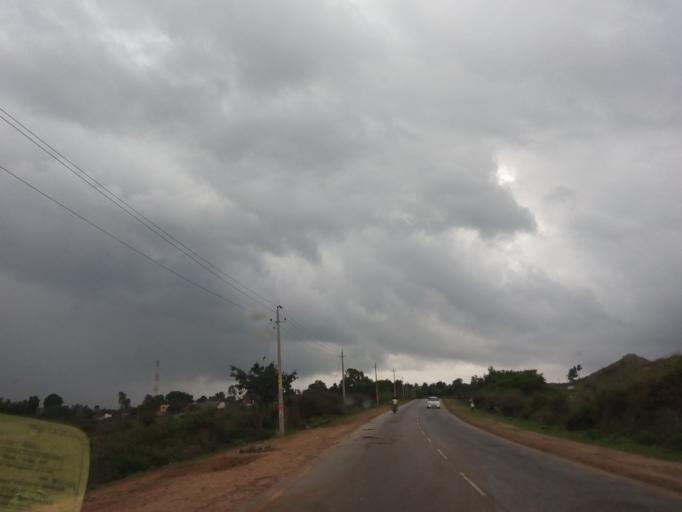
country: IN
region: Karnataka
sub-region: Hassan
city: Hassan
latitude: 13.0951
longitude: 76.0256
